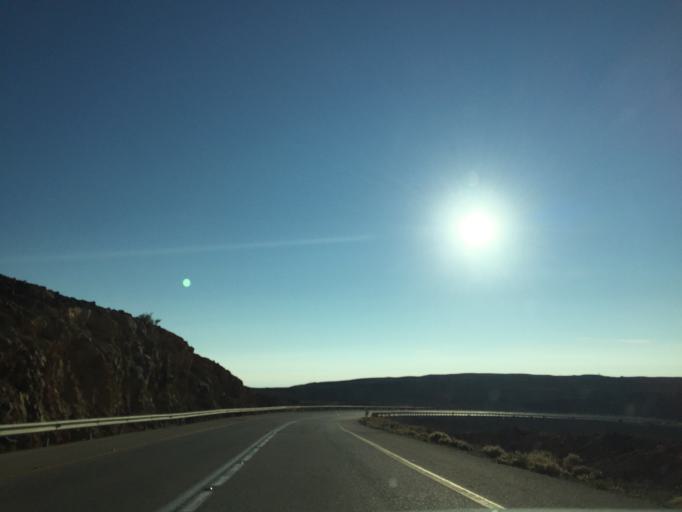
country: IL
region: Southern District
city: Mitzpe Ramon
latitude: 30.5067
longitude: 34.9437
